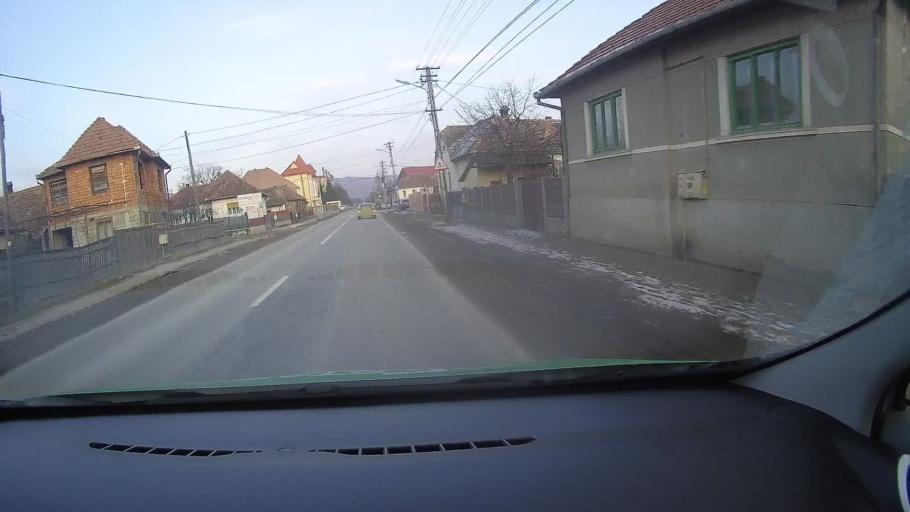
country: RO
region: Harghita
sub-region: Oras Cristuru Secuiesc
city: Cristuru Secuiesc
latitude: 46.2923
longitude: 25.0479
